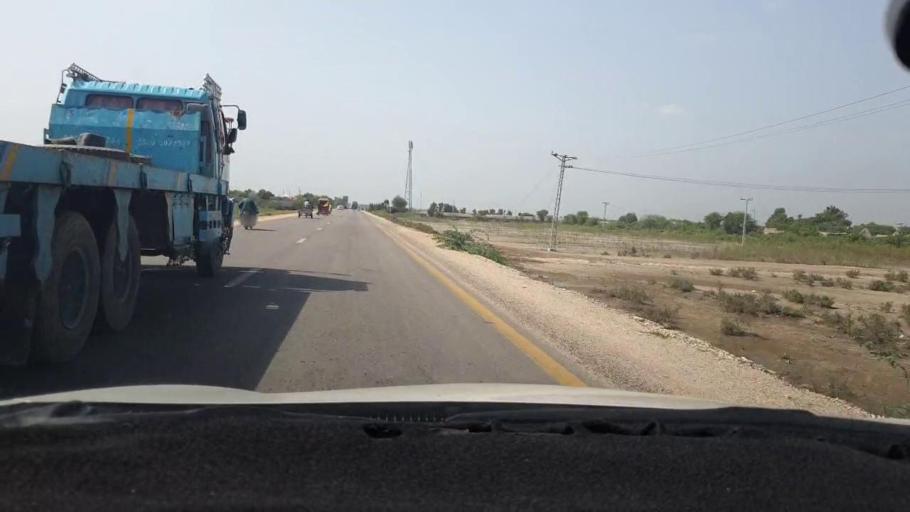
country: PK
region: Sindh
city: Mirpur Khas
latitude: 25.6852
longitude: 69.1129
